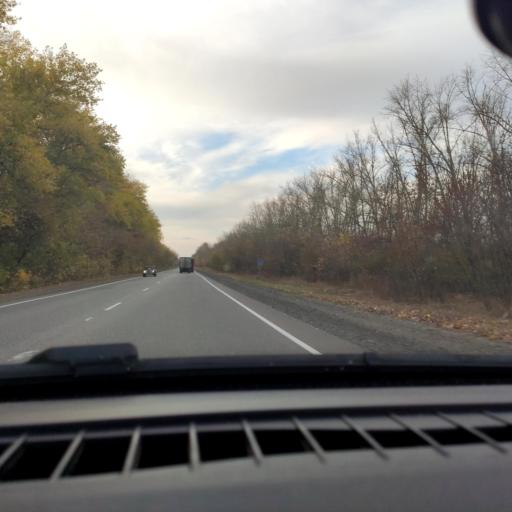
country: RU
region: Voronezj
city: Ostrogozhsk
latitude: 50.9558
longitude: 39.0357
